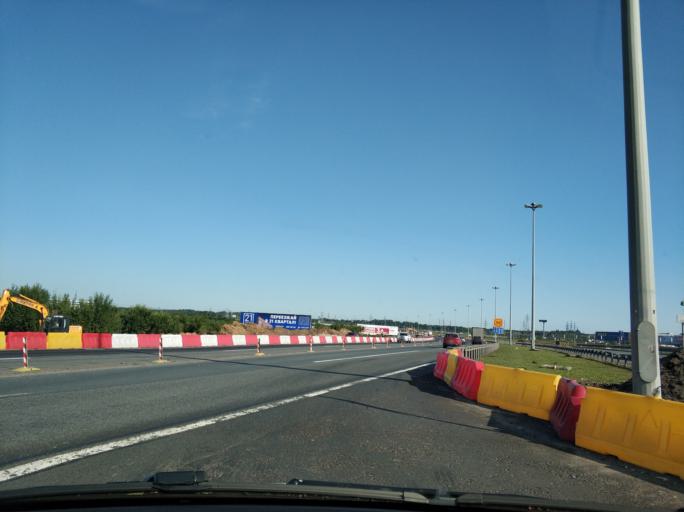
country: RU
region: Leningrad
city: Bugry
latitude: 60.0840
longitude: 30.3783
